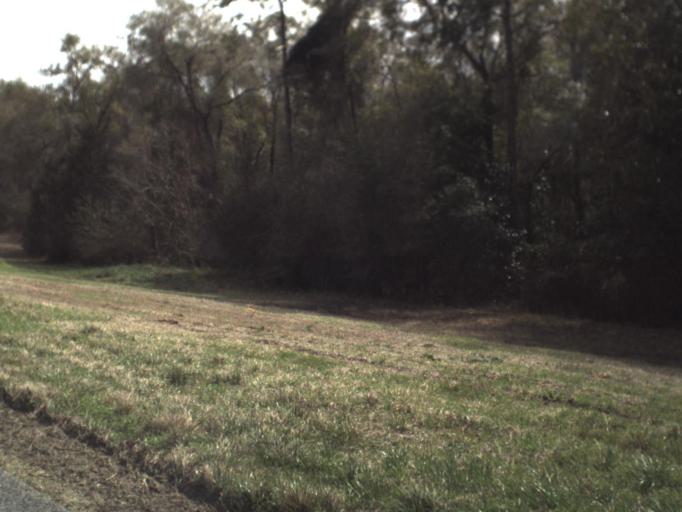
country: US
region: Florida
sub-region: Bay County
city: Youngstown
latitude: 30.5806
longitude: -85.3895
